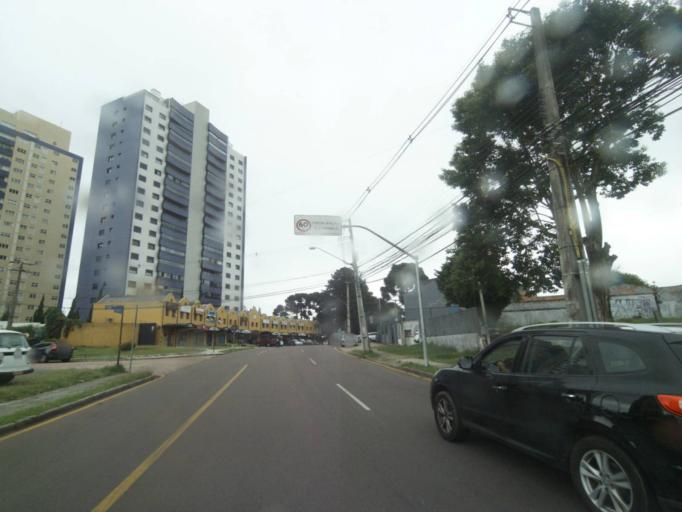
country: BR
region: Parana
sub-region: Curitiba
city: Curitiba
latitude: -25.4377
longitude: -49.3225
